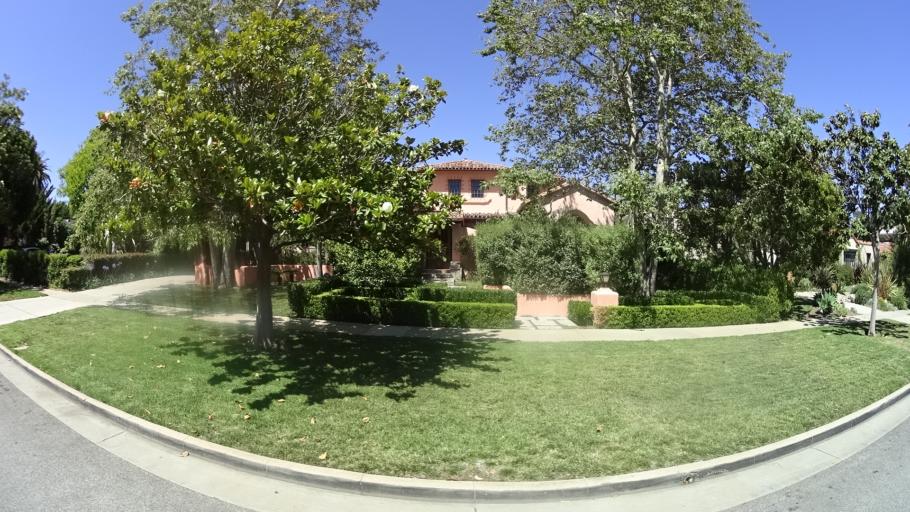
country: US
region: California
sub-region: Los Angeles County
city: Santa Monica
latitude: 34.0368
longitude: -118.4950
